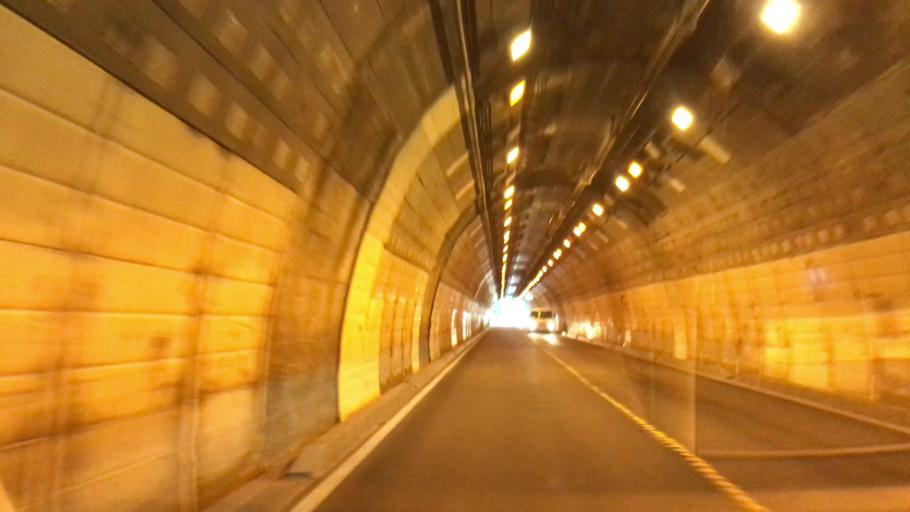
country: JP
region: Hokkaido
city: Iwanai
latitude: 43.0358
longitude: 140.6779
